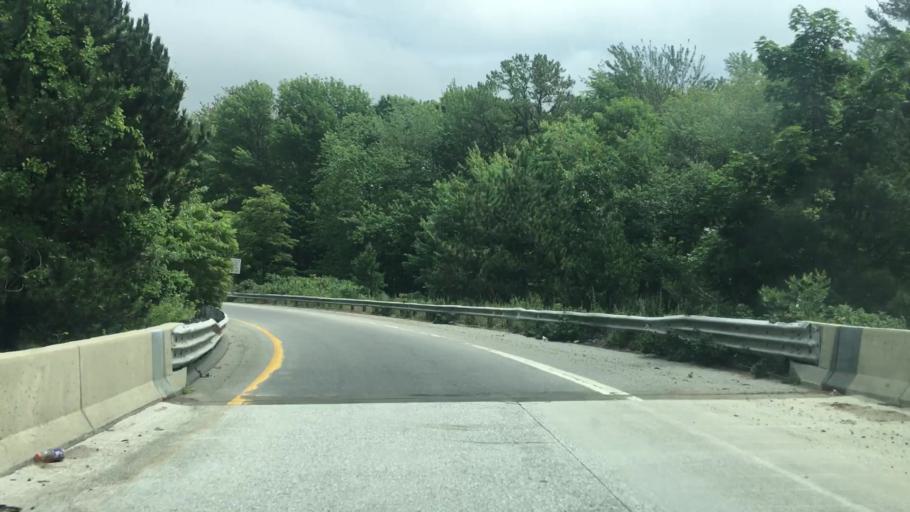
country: US
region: Maine
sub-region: Cumberland County
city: Brunswick
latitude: 43.9190
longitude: -69.9529
